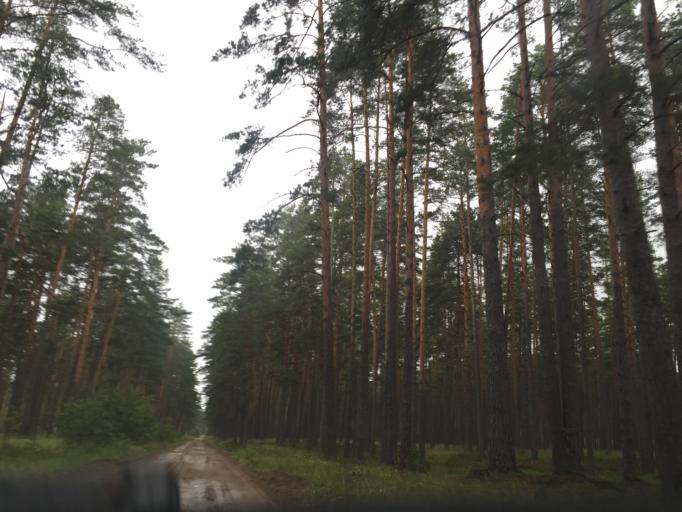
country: LV
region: Riga
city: Jaunciems
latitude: 57.0548
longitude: 24.2034
